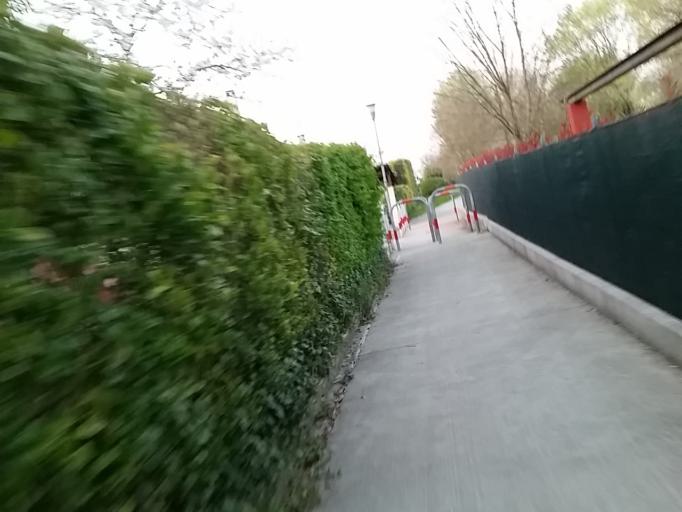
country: IT
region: Veneto
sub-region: Provincia di Padova
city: Mandriola-Sant'Agostino
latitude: 45.3657
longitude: 11.8480
